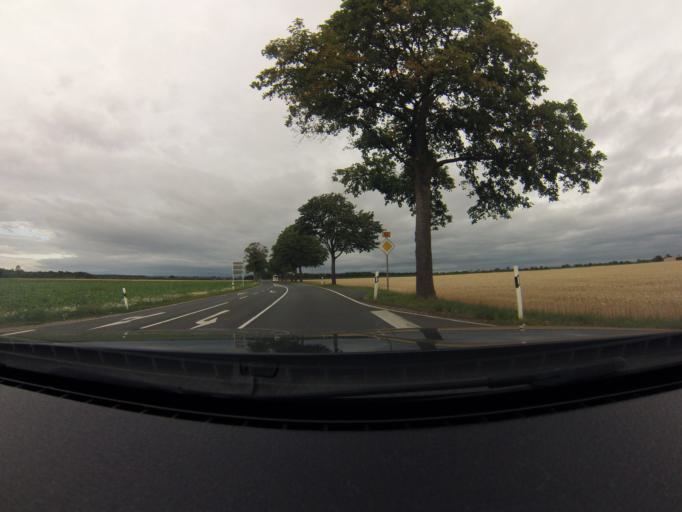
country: DE
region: North Rhine-Westphalia
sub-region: Regierungsbezirk Koln
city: Rheinbach
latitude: 50.6781
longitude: 6.9405
